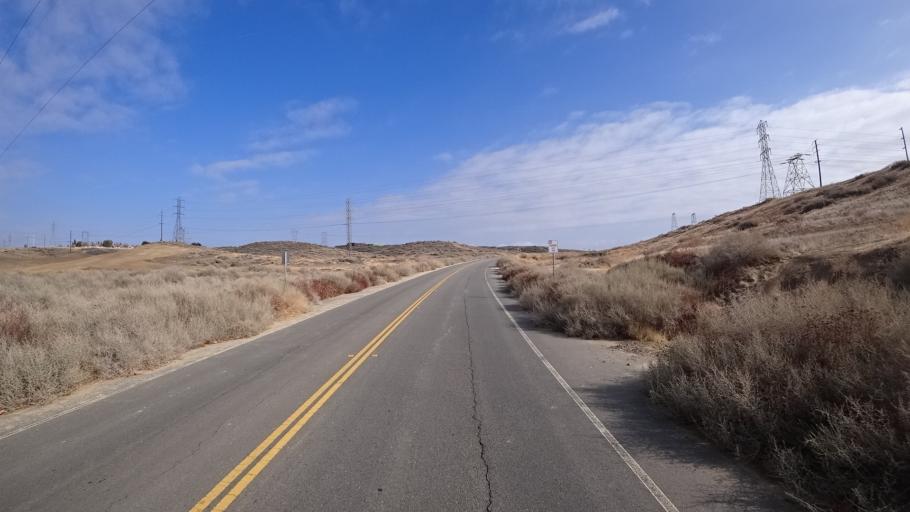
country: US
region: California
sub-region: Kern County
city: Bakersfield
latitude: 35.3918
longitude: -118.9244
